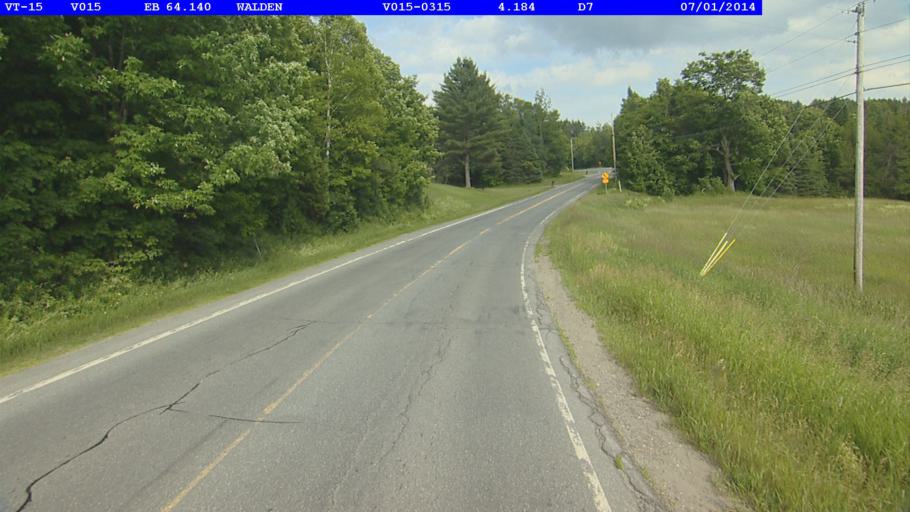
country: US
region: Vermont
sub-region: Caledonia County
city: Hardwick
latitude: 44.4483
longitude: -72.2438
